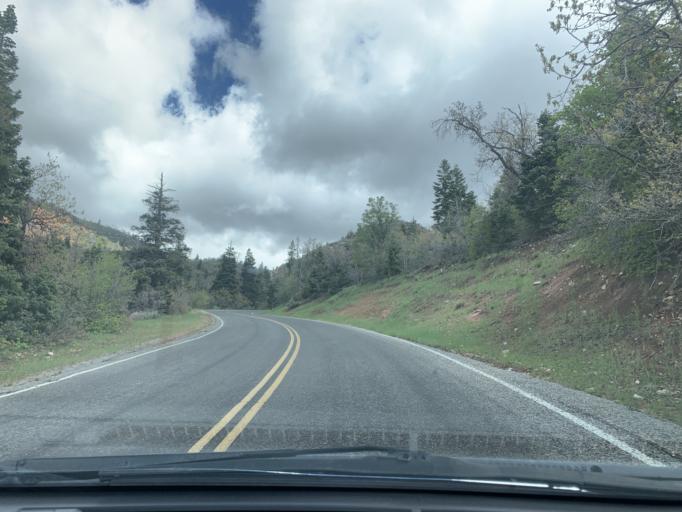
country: US
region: Utah
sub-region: Sanpete County
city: Fountain Green
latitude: 39.7878
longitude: -111.6886
